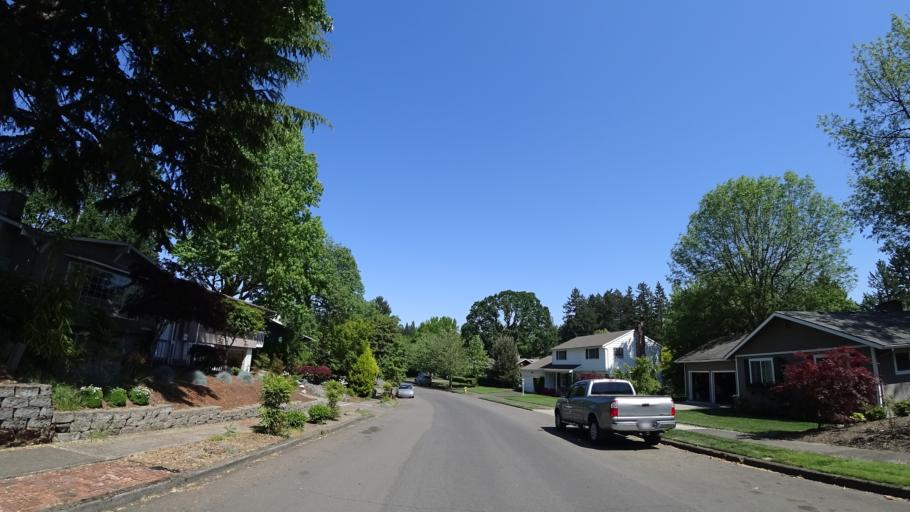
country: US
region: Oregon
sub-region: Washington County
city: Cedar Hills
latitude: 45.4970
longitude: -122.7952
